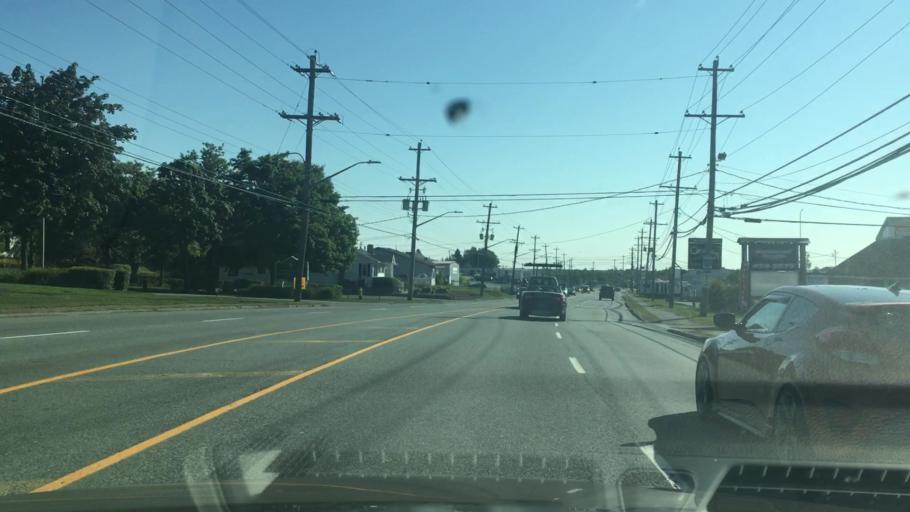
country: CA
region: Nova Scotia
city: Cole Harbour
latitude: 44.6982
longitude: -63.4918
